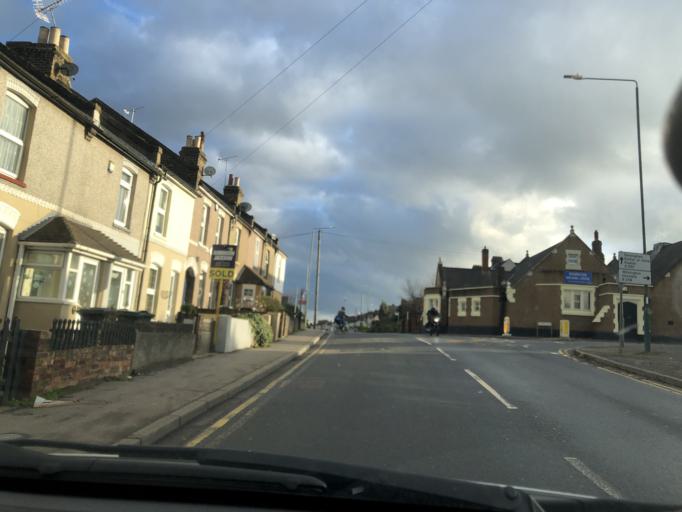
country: GB
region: England
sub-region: Kent
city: Dartford
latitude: 51.4336
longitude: 0.2158
